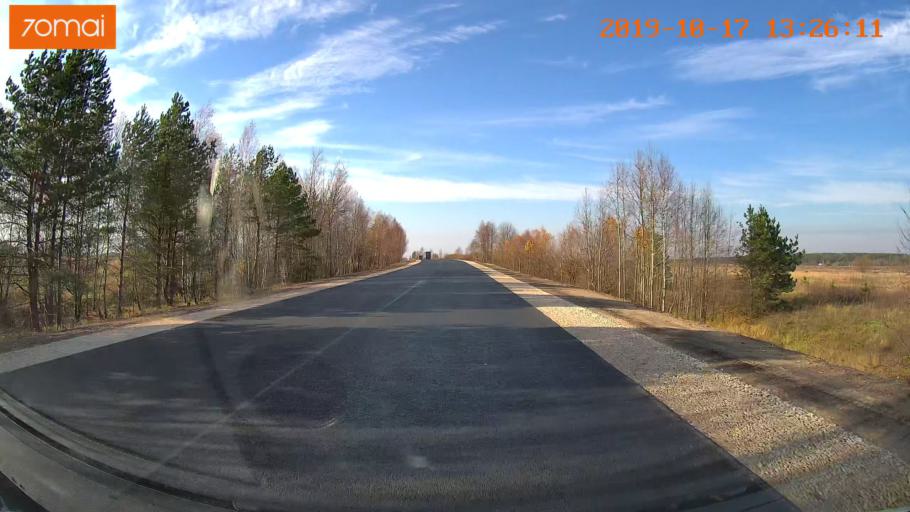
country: RU
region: Rjazan
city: Gus'-Zheleznyy
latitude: 55.1086
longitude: 40.9274
